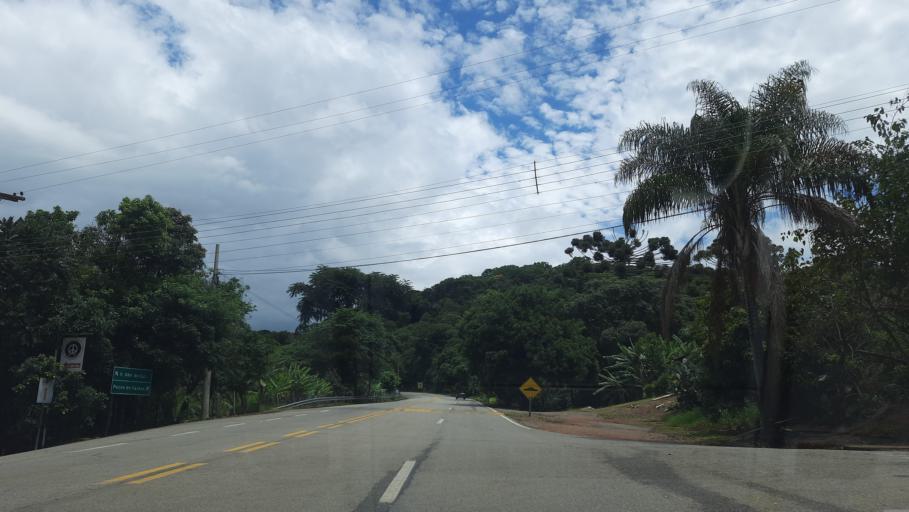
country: BR
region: Sao Paulo
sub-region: Sao Joao Da Boa Vista
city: Sao Joao da Boa Vista
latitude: -21.8363
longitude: -46.7426
